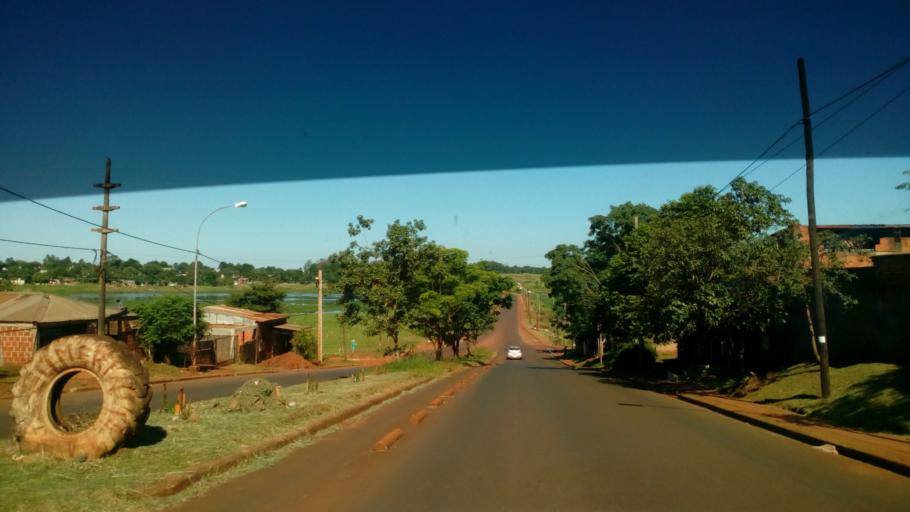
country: AR
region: Misiones
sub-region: Departamento de Capital
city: Posadas
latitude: -27.4284
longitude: -55.9095
